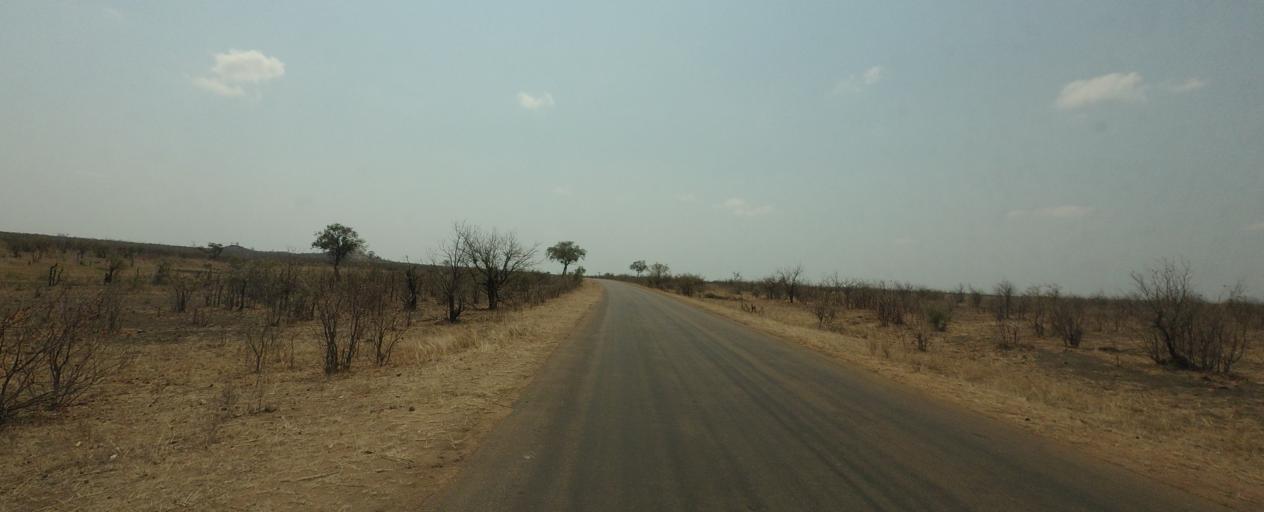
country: ZA
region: Limpopo
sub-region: Mopani District Municipality
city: Phalaborwa
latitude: -23.5042
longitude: 31.4044
